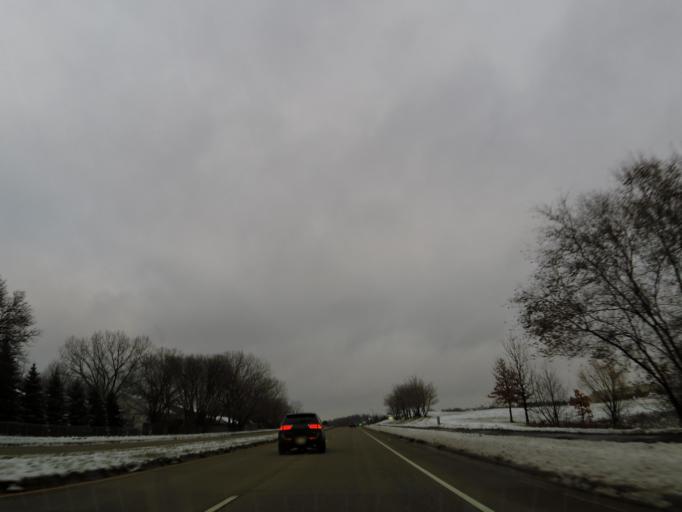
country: US
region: Minnesota
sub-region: Dakota County
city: Apple Valley
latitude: 44.7137
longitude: -93.2673
